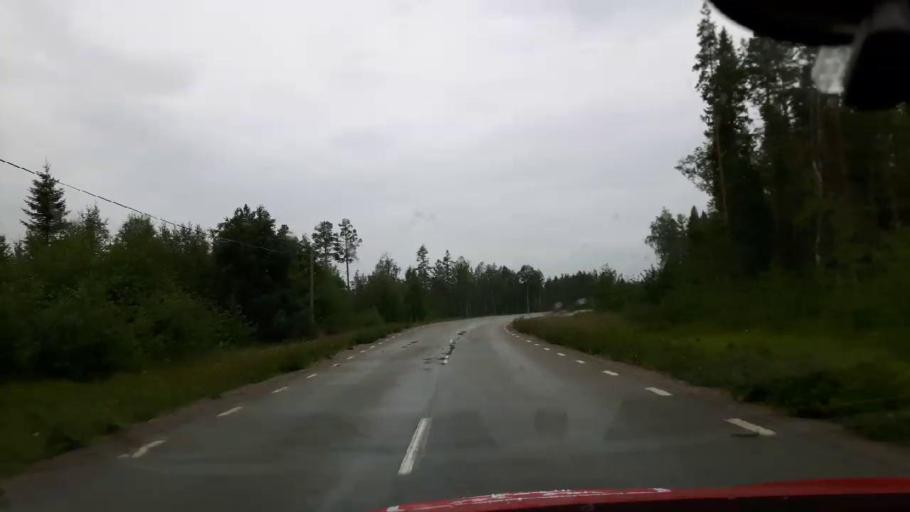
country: SE
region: Jaemtland
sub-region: OEstersunds Kommun
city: Brunflo
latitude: 62.8211
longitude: 14.9983
